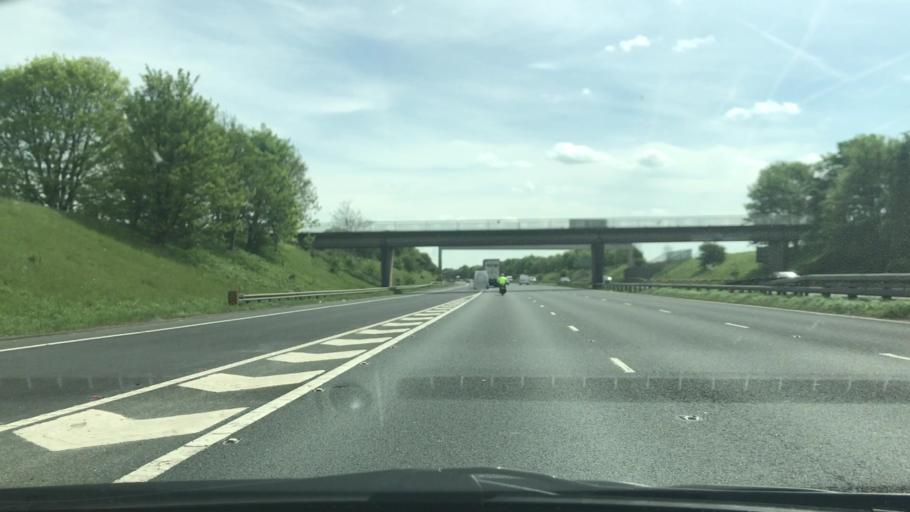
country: GB
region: England
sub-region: City and Borough of Wakefield
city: Knottingley
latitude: 53.6940
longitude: -1.2588
